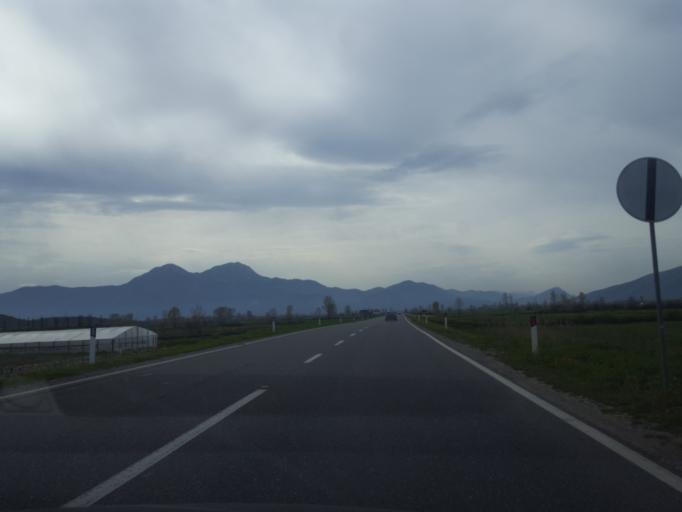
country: AL
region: Lezhe
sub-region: Rrethi i Lezhes
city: Dajc
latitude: 41.9092
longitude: 19.6005
